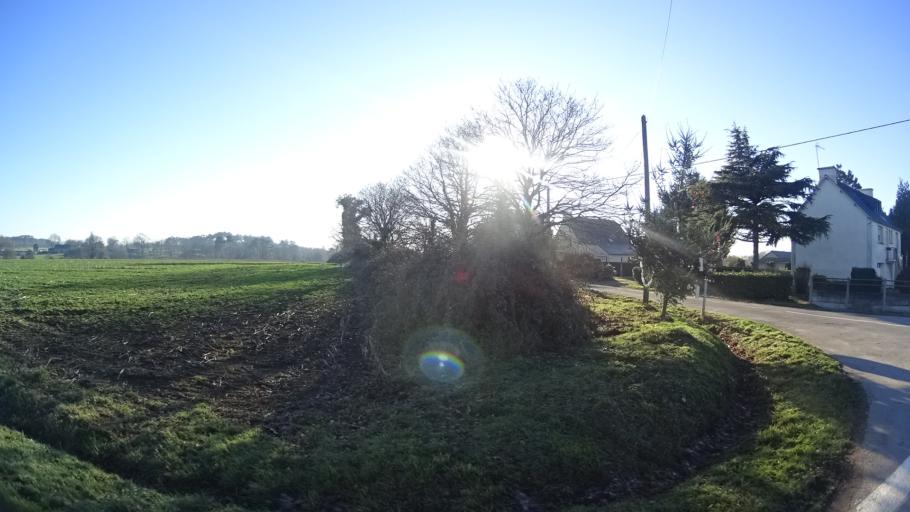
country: FR
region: Brittany
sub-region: Departement du Morbihan
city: Allaire
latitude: 47.6559
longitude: -2.1732
